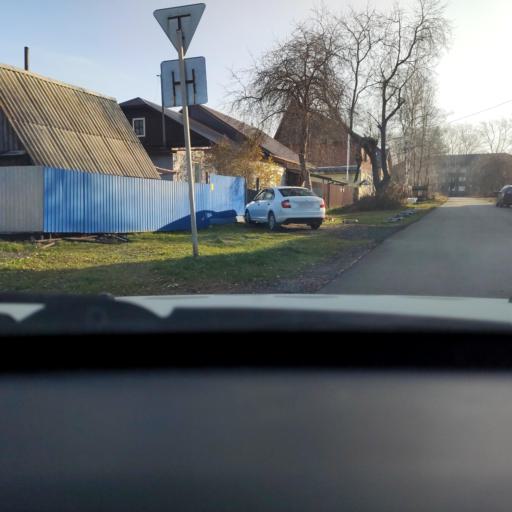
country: RU
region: Perm
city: Perm
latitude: 58.0898
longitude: 56.3870
